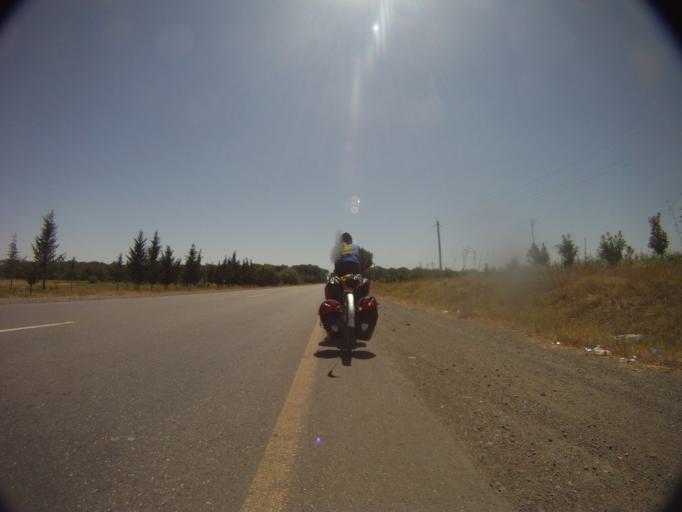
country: AZ
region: Tovuz
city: Qaraxanli
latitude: 41.0362
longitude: 45.5894
